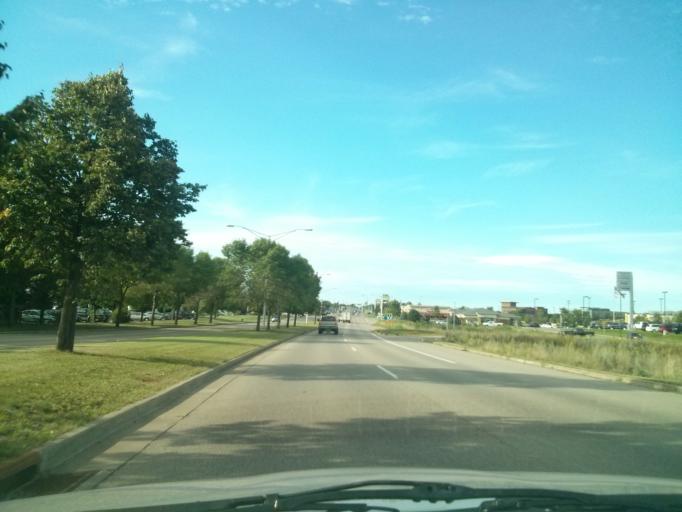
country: US
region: Wisconsin
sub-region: Saint Croix County
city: Hudson
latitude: 44.9557
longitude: -92.7213
